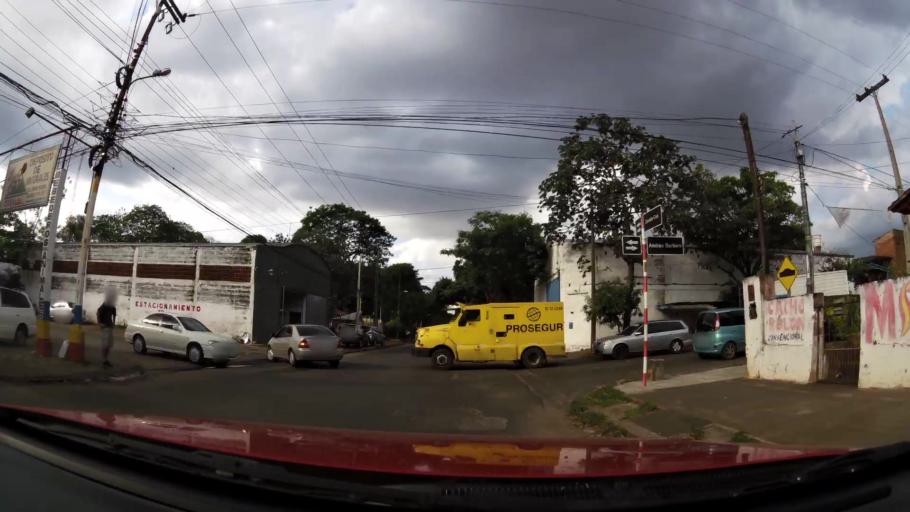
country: PY
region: Central
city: Fernando de la Mora
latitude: -25.3382
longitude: -57.5631
